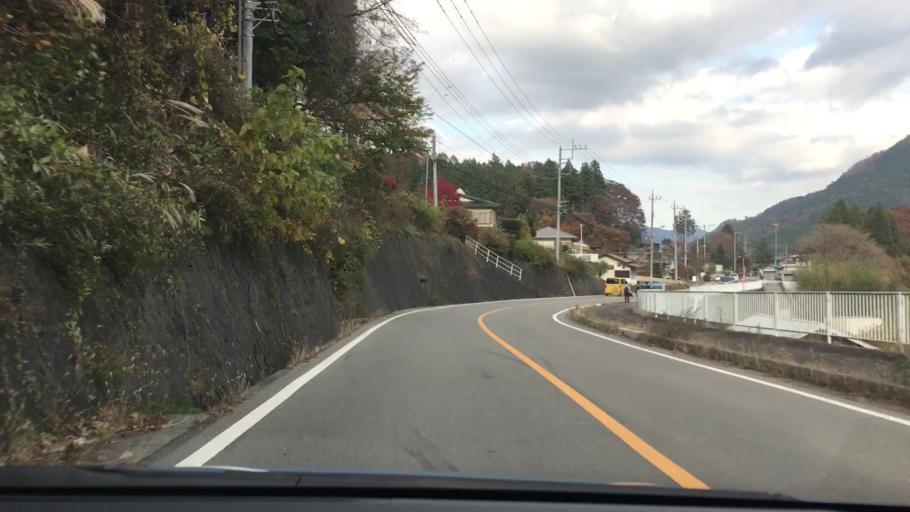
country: JP
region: Yamanashi
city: Otsuki
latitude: 35.4933
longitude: 138.9775
